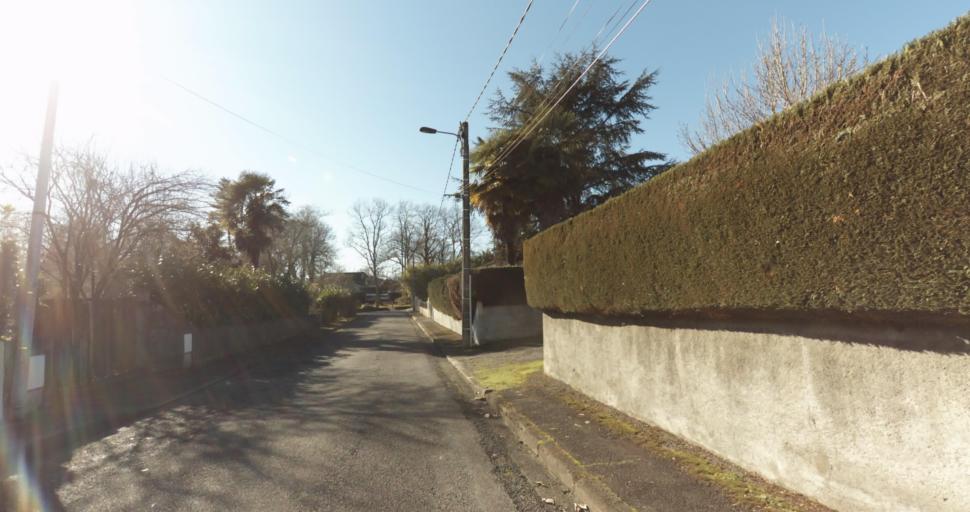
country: FR
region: Aquitaine
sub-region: Departement des Pyrenees-Atlantiques
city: Buros
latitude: 43.3273
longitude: -0.2916
